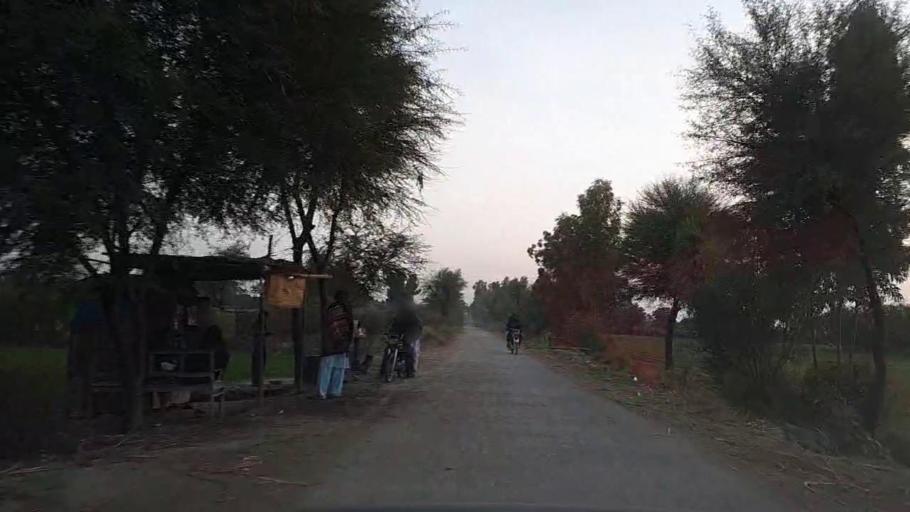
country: PK
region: Sindh
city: Tando Mittha Khan
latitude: 25.9451
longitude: 69.1546
